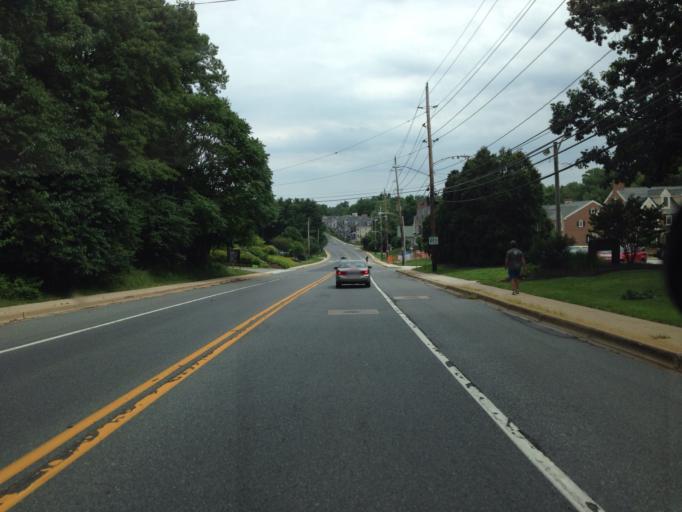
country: US
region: Delaware
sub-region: New Castle County
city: Newark
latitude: 39.6899
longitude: -75.7606
